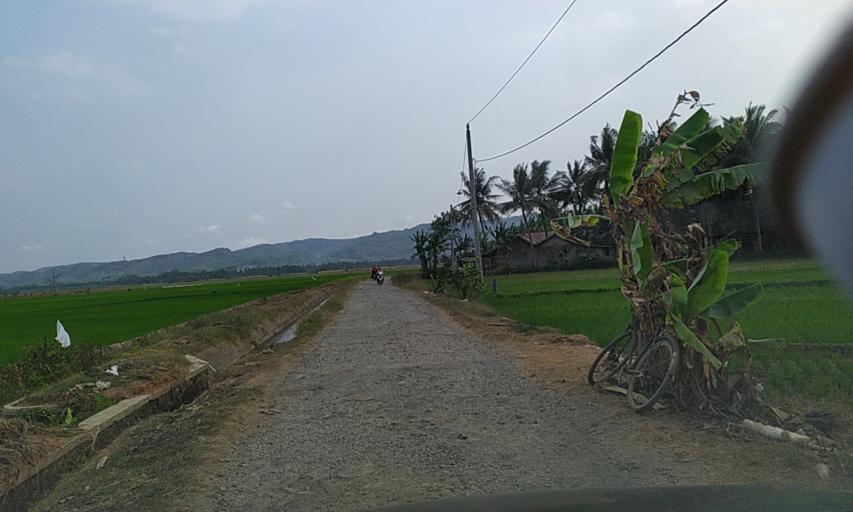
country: ID
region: Central Java
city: Mulyadadi
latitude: -7.3410
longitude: 108.7559
